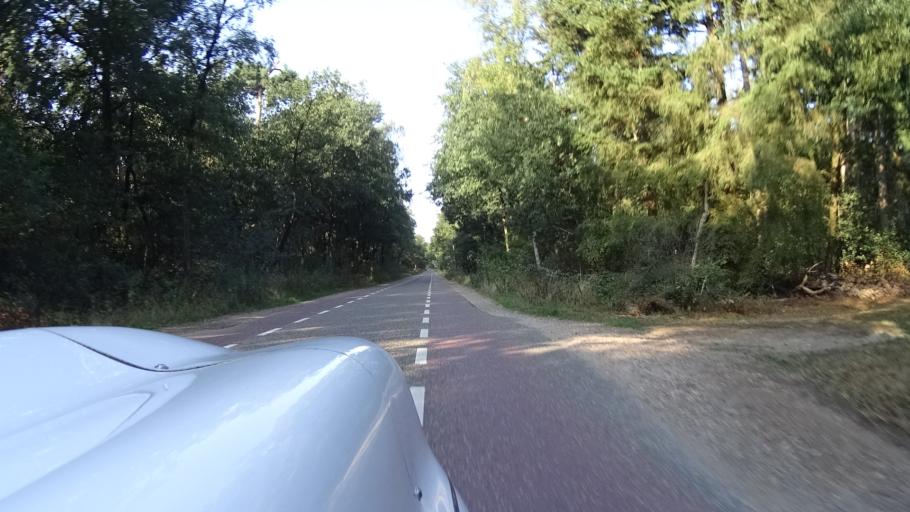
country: NL
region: Limburg
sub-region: Gemeente Bergen
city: Wellerlooi
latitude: 51.5416
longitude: 6.1515
